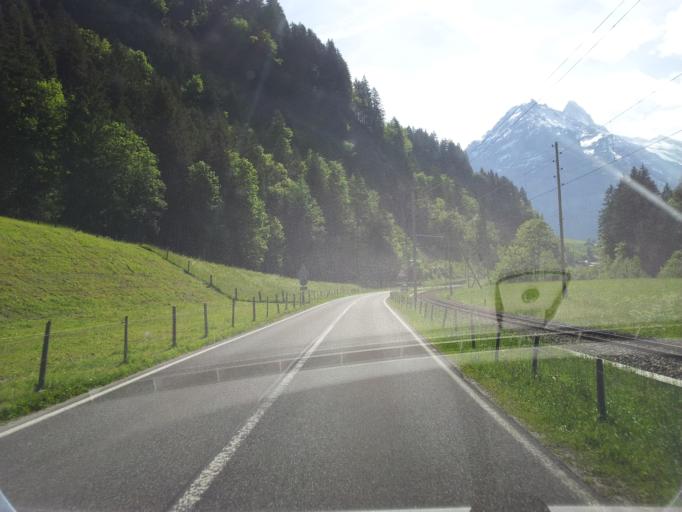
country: CH
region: Bern
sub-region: Interlaken-Oberhasli District
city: Grindelwald
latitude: 46.6358
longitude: 7.9914
